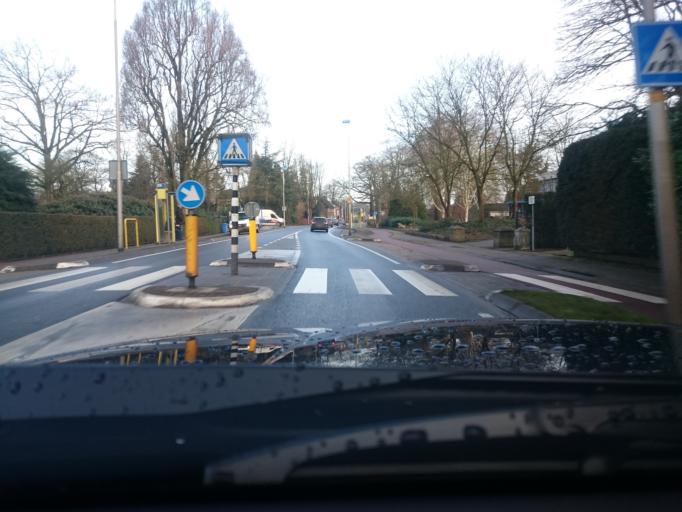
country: NL
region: Gelderland
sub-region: Gemeente Voorst
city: Voorst
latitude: 52.1696
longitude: 6.1430
